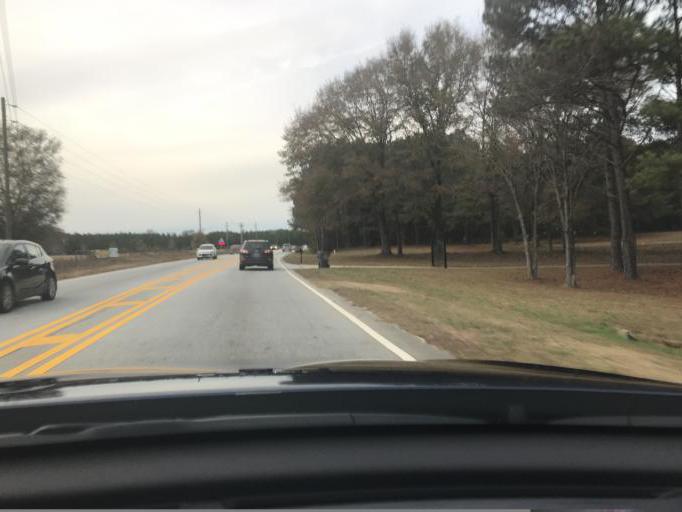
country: US
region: Georgia
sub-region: Newton County
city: Porterdale
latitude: 33.5965
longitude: -83.9155
